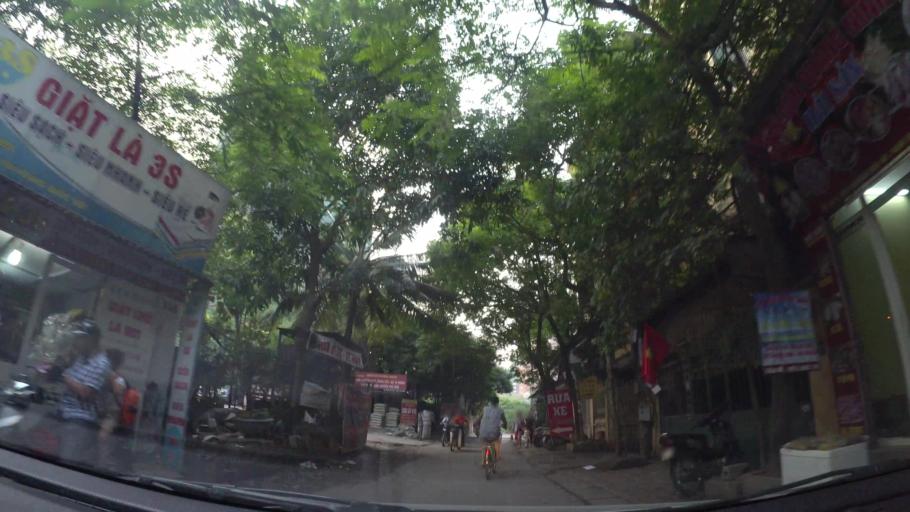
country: VN
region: Ha Noi
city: Cau Giay
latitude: 21.0492
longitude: 105.7942
